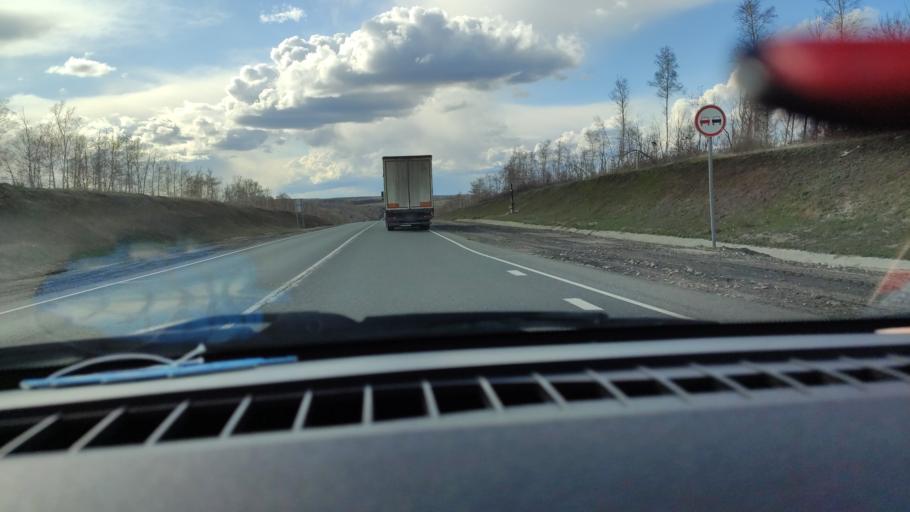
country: RU
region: Saratov
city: Shikhany
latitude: 52.1237
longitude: 47.2517
